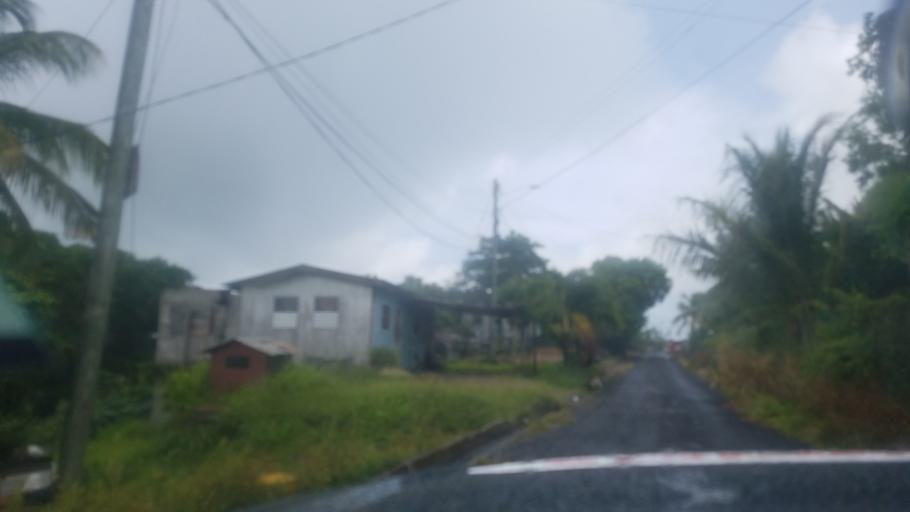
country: LC
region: Laborie Quarter
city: Laborie
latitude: 13.7486
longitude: -60.9618
